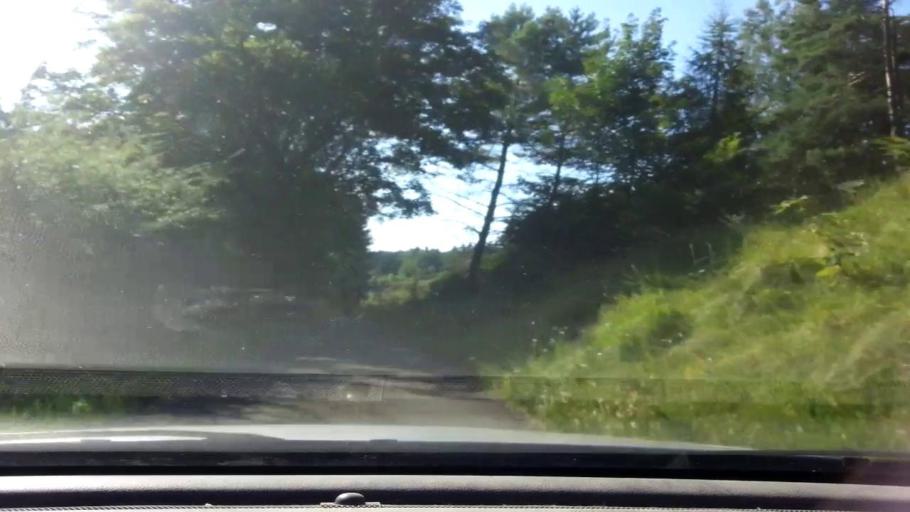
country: DE
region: Bavaria
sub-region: Upper Franconia
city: Wattendorf
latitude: 50.0043
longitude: 11.1072
